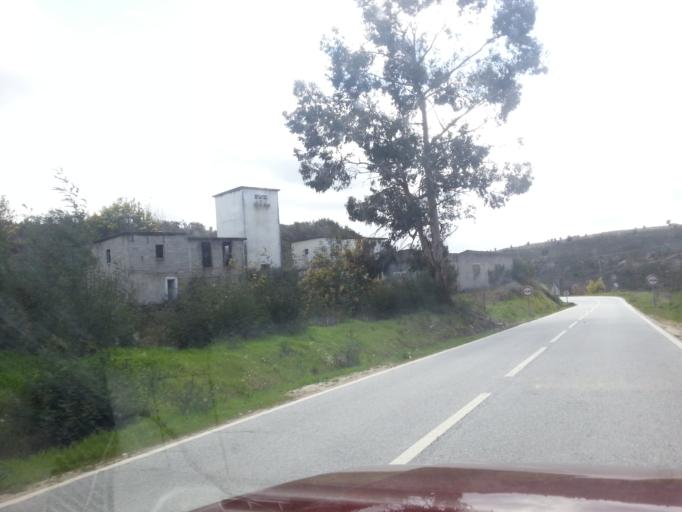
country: PT
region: Guarda
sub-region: Fornos de Algodres
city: Fornos de Algodres
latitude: 40.6010
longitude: -7.5279
